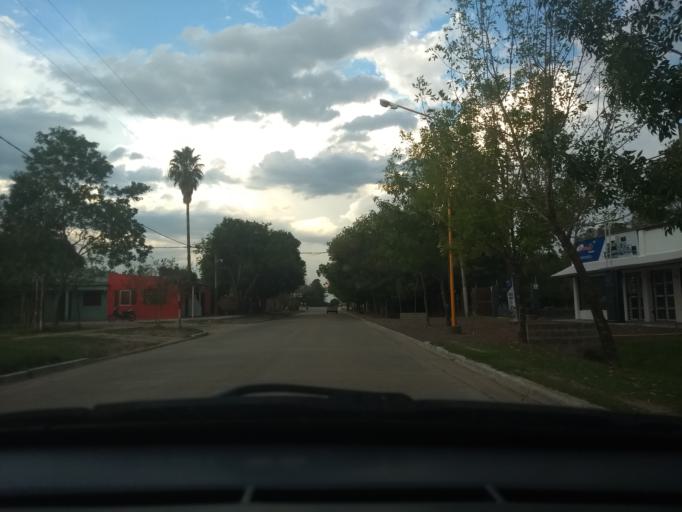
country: AR
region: Corrientes
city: Riachuelo
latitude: -27.5824
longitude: -58.7420
